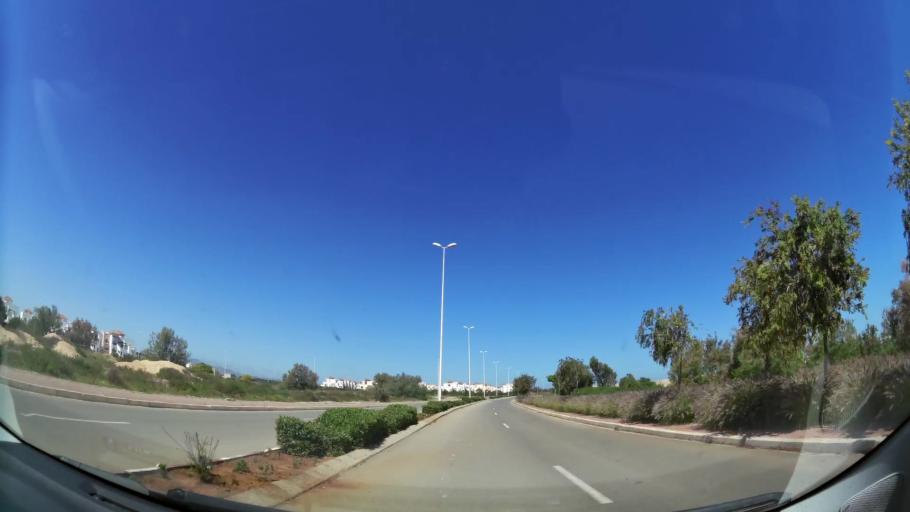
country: MA
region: Oriental
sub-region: Berkane-Taourirt
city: Madagh
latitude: 35.1036
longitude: -2.3064
